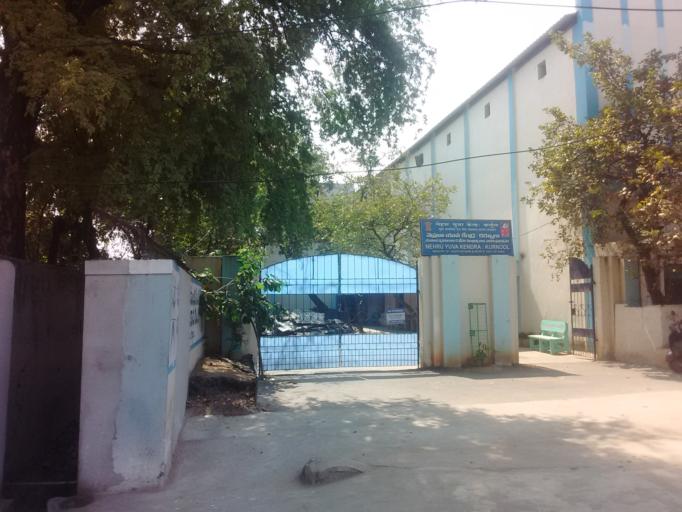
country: IN
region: Telangana
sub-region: Mahbubnagar
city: Alampur
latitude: 15.8321
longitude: 78.0444
